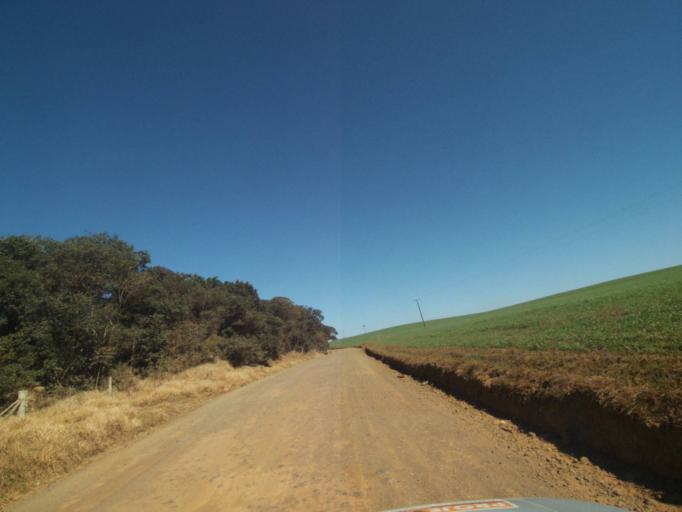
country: BR
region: Parana
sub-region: Tibagi
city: Tibagi
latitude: -24.6150
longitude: -50.6063
